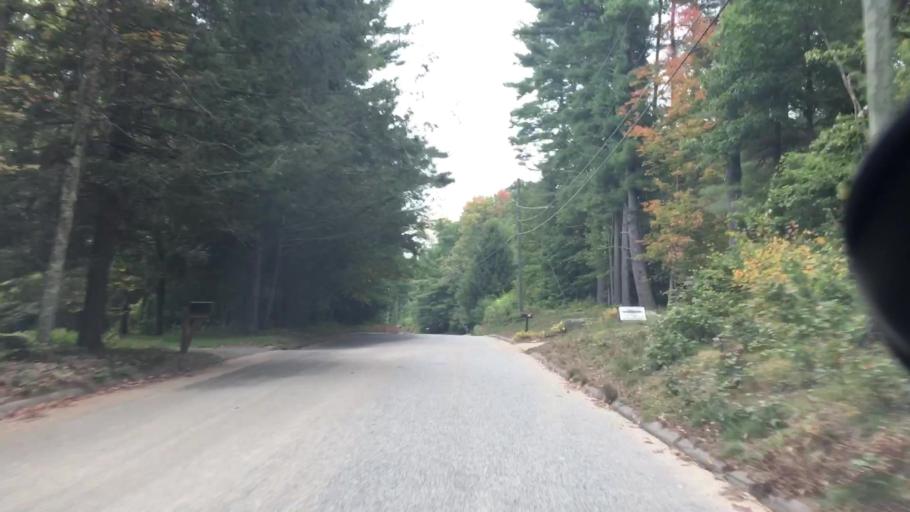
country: US
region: Connecticut
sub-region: Tolland County
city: Stafford Springs
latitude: 41.9805
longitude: -72.3279
